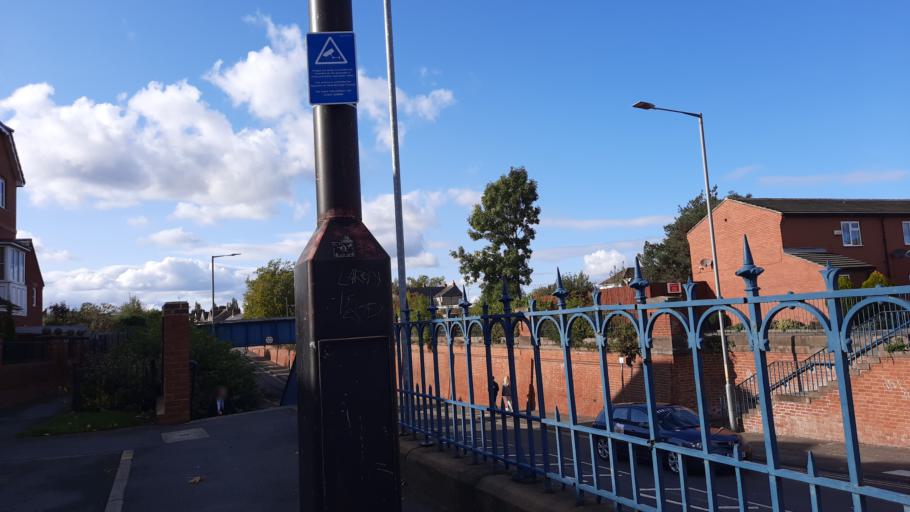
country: GB
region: England
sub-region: Stockton-on-Tees
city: Stockton-on-Tees
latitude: 54.5609
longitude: -1.3236
